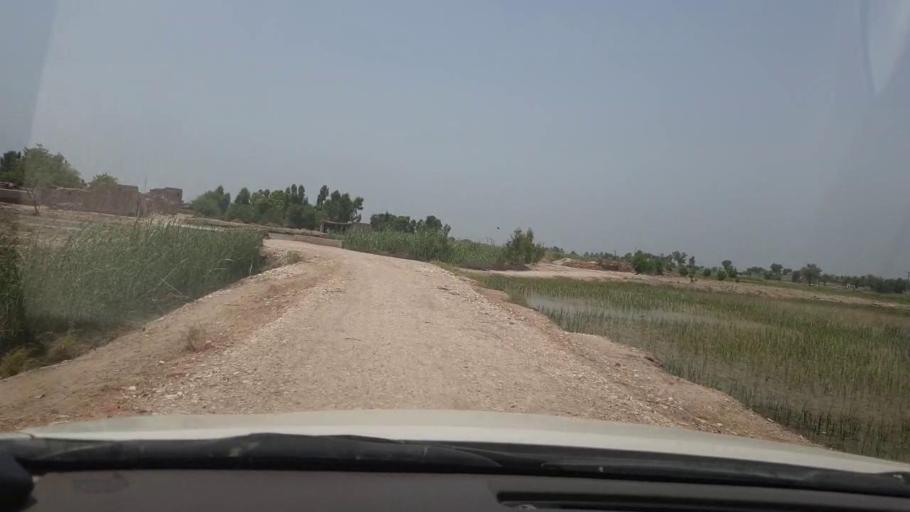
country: PK
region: Sindh
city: Garhi Yasin
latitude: 27.9058
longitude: 68.5506
